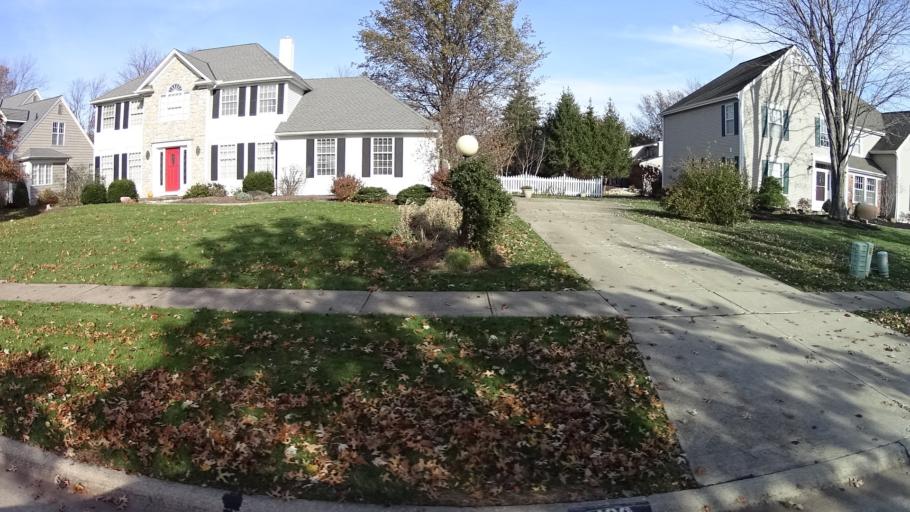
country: US
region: Ohio
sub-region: Lorain County
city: Avon Lake
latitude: 41.4952
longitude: -81.9807
